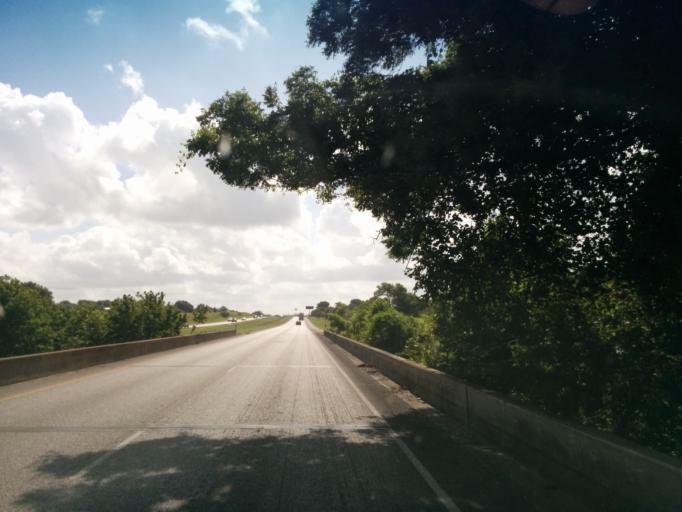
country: US
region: Texas
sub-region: Fayette County
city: Schulenburg
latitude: 29.6895
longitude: -96.9385
